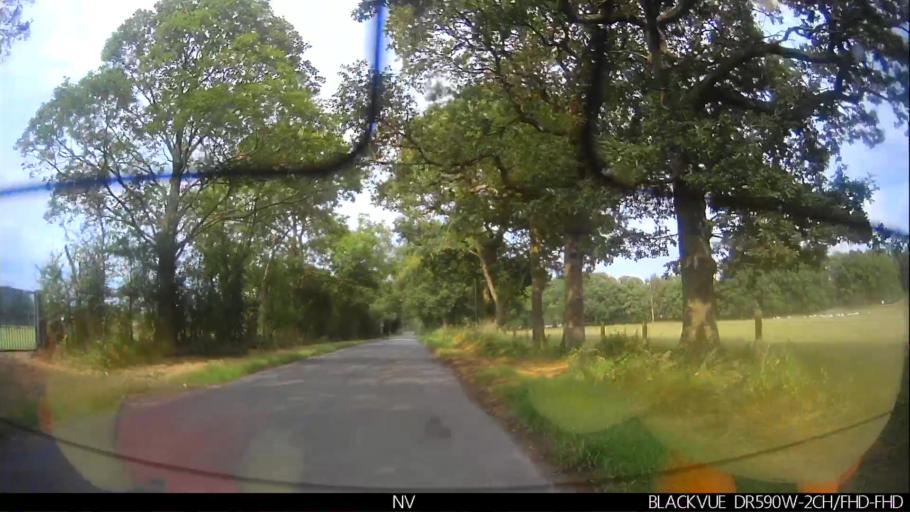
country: GB
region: England
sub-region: North Yorkshire
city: Strensall
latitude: 54.0415
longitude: -1.0137
